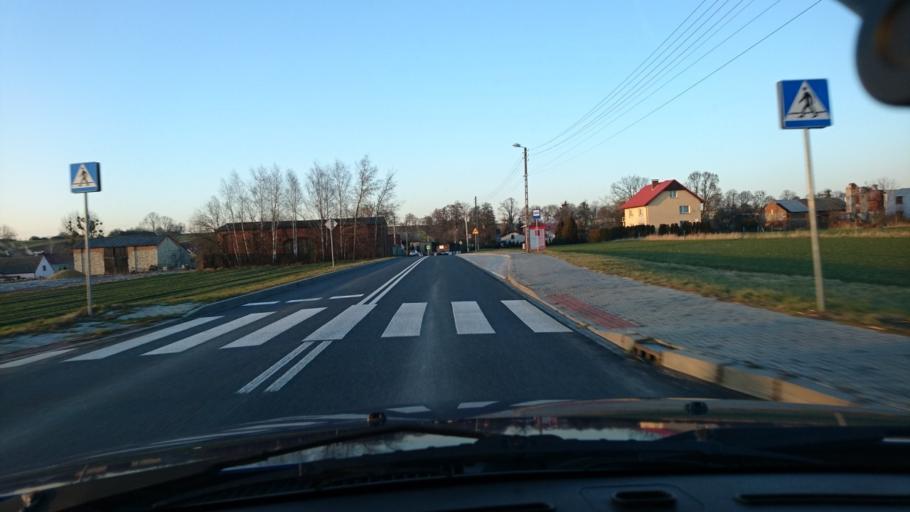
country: PL
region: Silesian Voivodeship
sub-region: Powiat gliwicki
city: Wielowies
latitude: 50.4743
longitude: 18.6087
